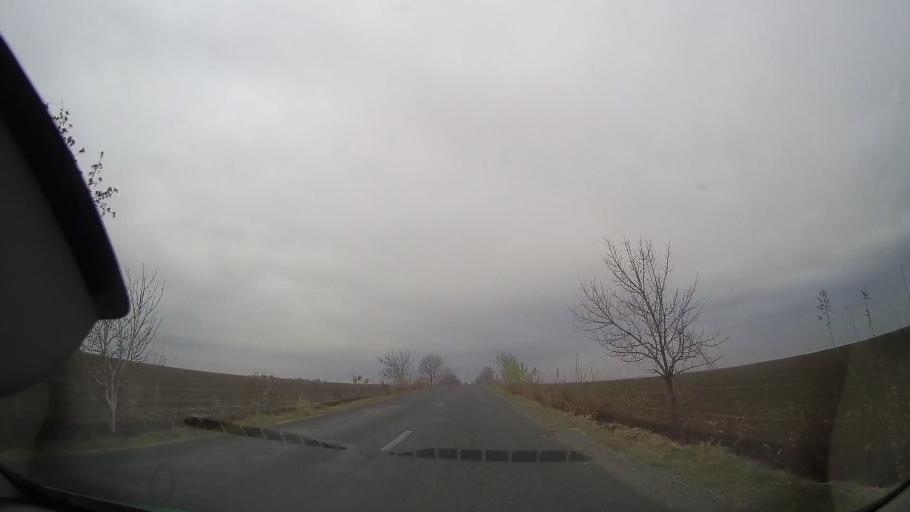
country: RO
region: Buzau
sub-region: Comuna Padina
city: Padina
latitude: 44.7815
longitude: 27.1515
